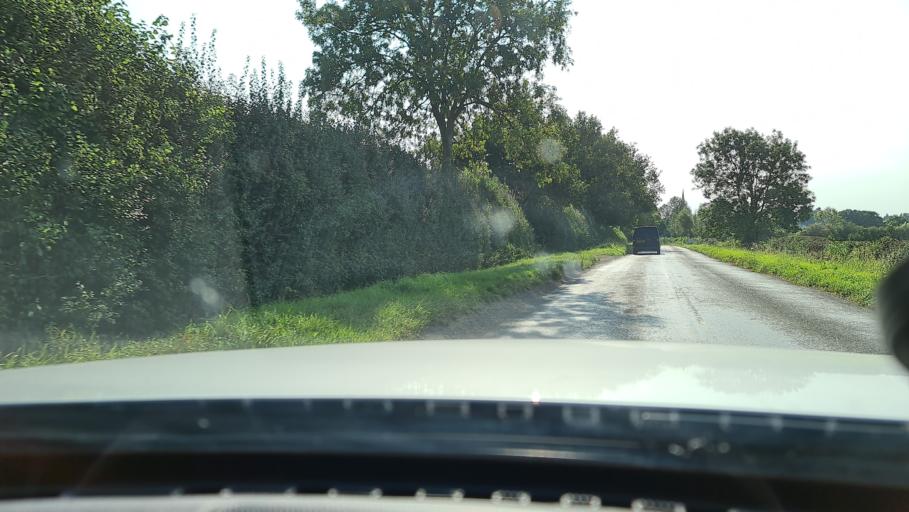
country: GB
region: England
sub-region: Oxfordshire
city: Adderbury
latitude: 52.0290
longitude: -1.2815
